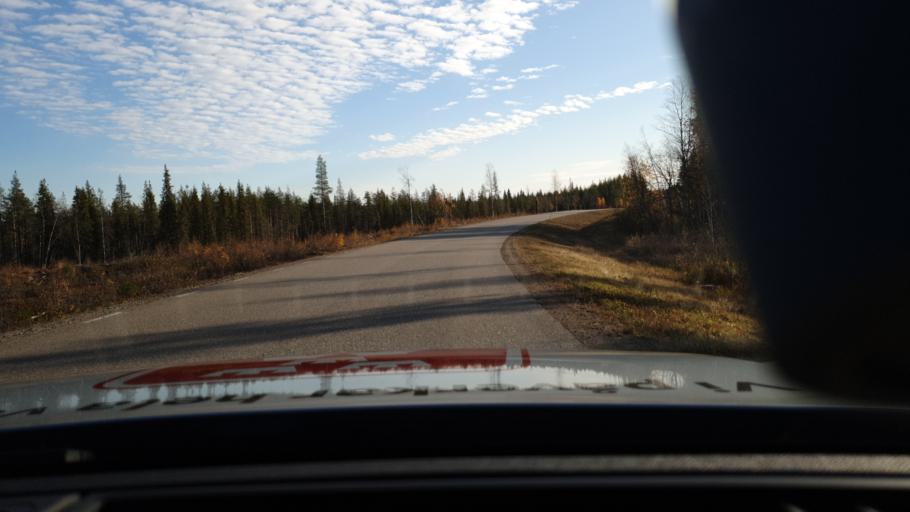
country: SE
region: Norrbotten
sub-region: Gallivare Kommun
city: Malmberget
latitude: 67.1306
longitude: 21.4192
